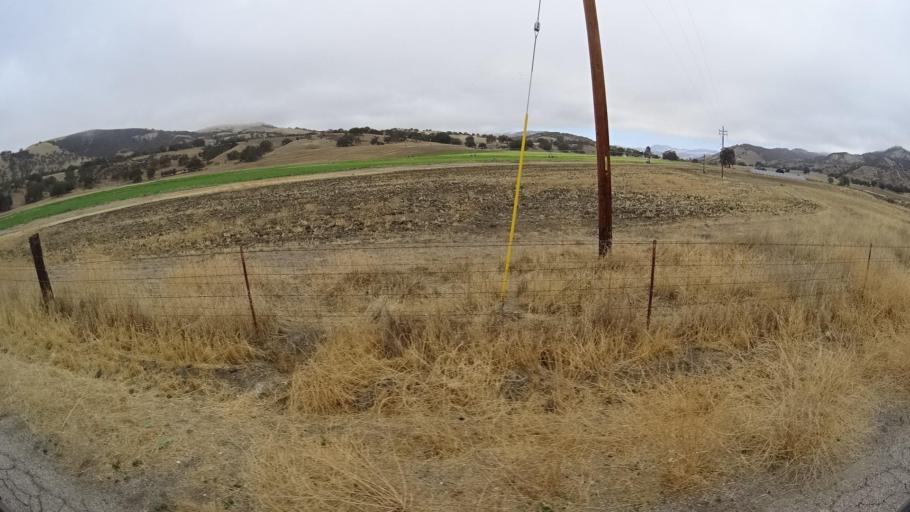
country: US
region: California
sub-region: San Luis Obispo County
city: San Miguel
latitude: 35.9063
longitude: -120.6943
